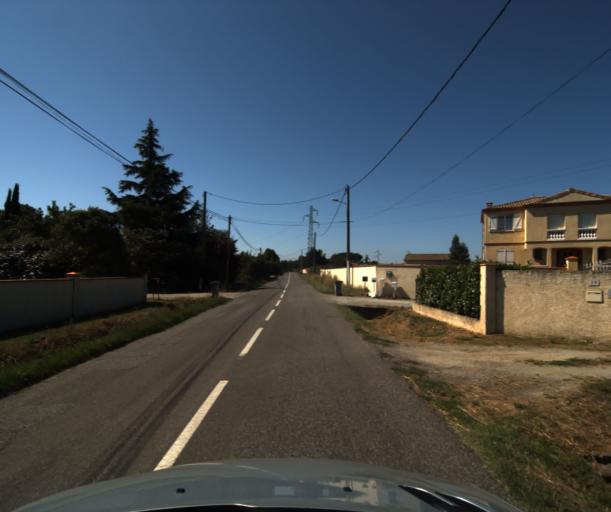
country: FR
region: Midi-Pyrenees
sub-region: Departement de la Haute-Garonne
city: Saubens
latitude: 43.4903
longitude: 1.3520
